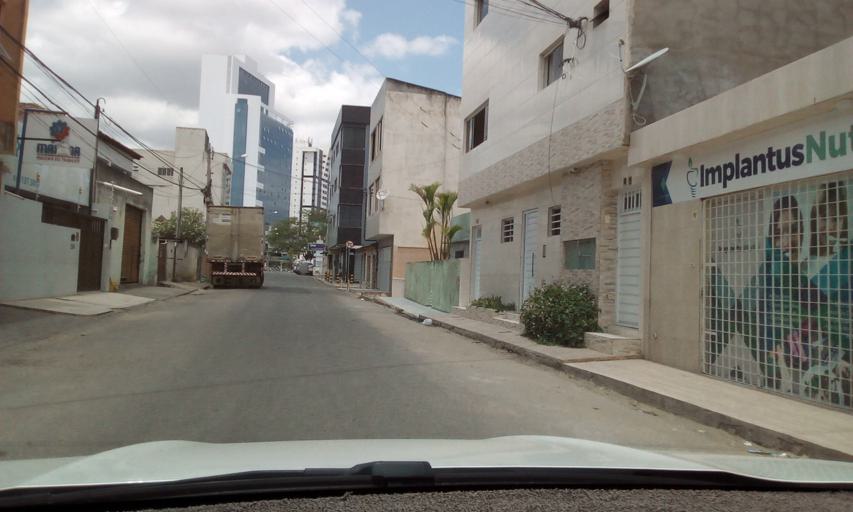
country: BR
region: Pernambuco
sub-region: Caruaru
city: Caruaru
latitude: -8.2712
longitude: -35.9779
